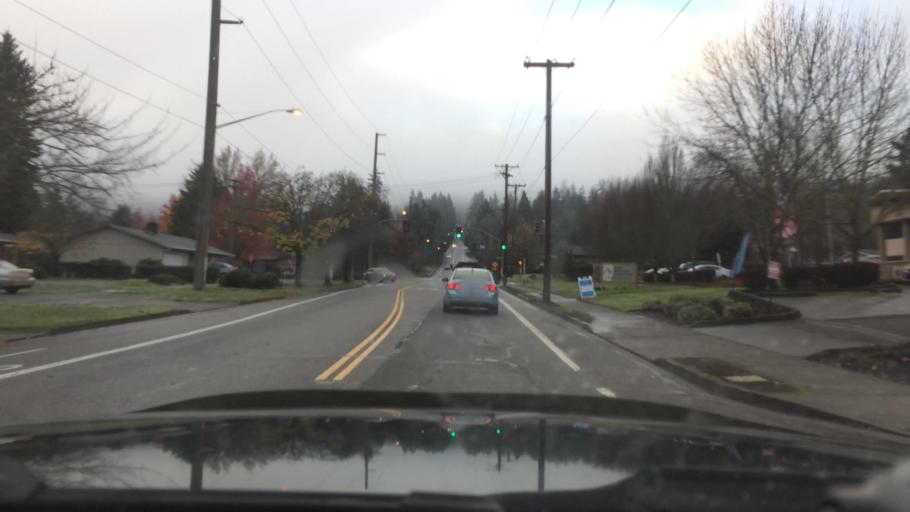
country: US
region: Oregon
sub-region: Lane County
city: Eugene
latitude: 44.0341
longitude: -123.1179
